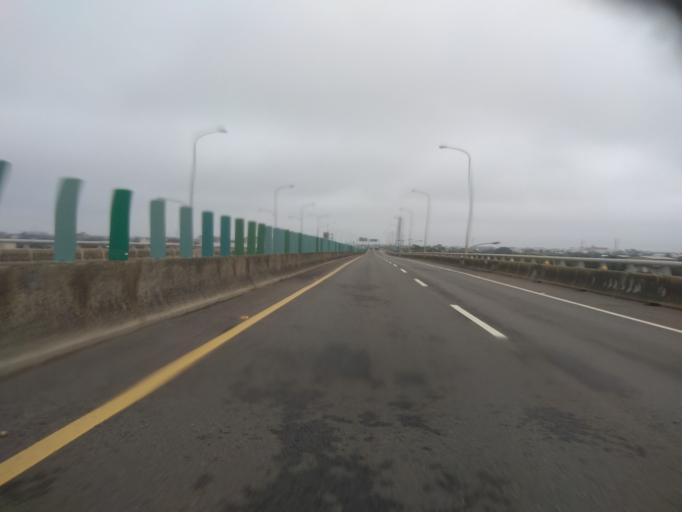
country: TW
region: Taiwan
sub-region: Hsinchu
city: Zhubei
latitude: 25.0002
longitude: 121.1006
